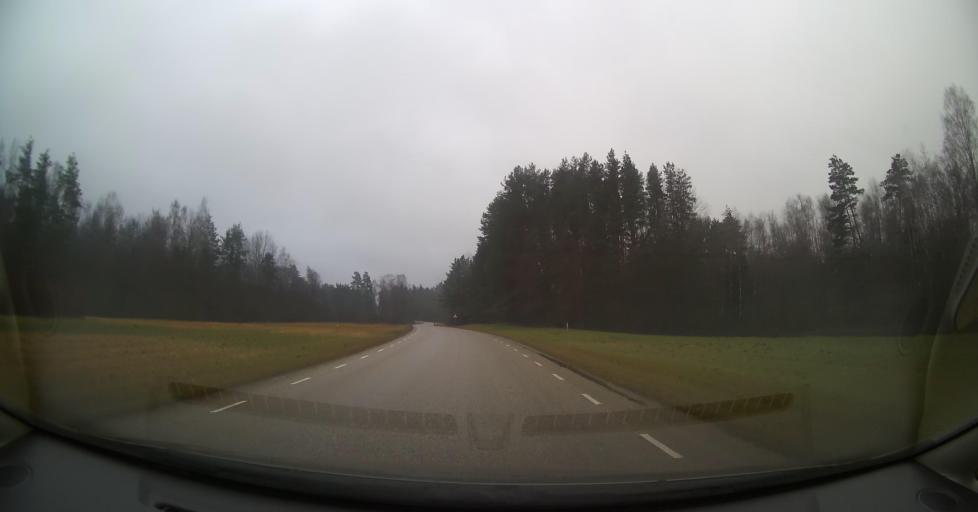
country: EE
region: Tartu
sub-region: Tartu linn
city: Tartu
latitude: 58.3524
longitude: 26.8034
